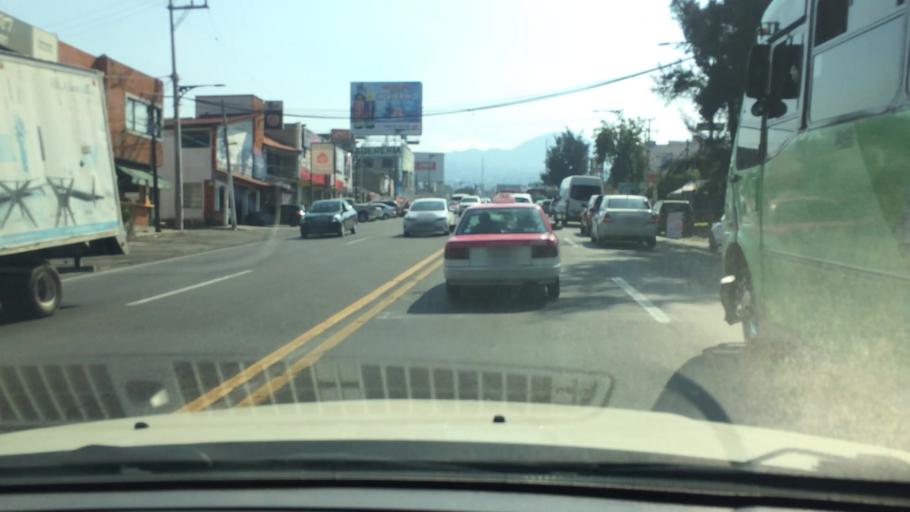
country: MX
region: Mexico City
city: Tlalpan
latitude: 19.2696
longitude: -99.1706
